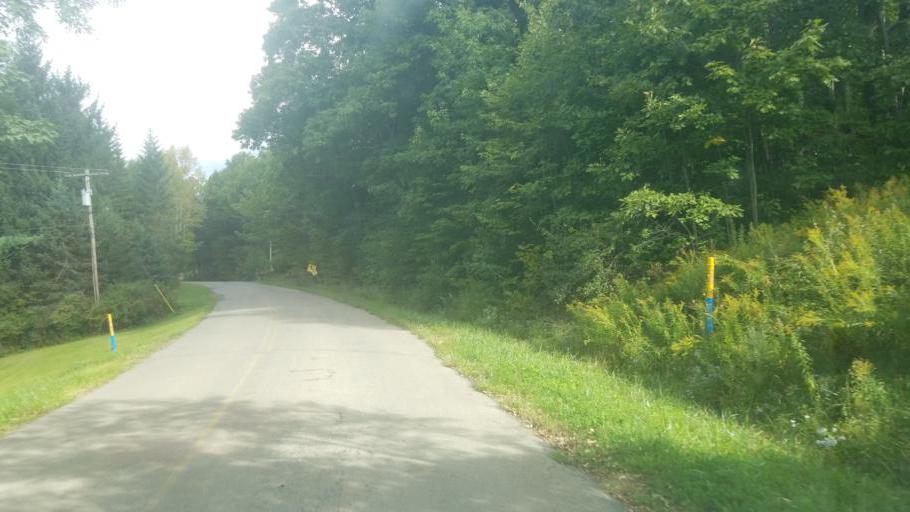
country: US
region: New York
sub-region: Cattaraugus County
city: Weston Mills
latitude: 42.1596
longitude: -78.3618
